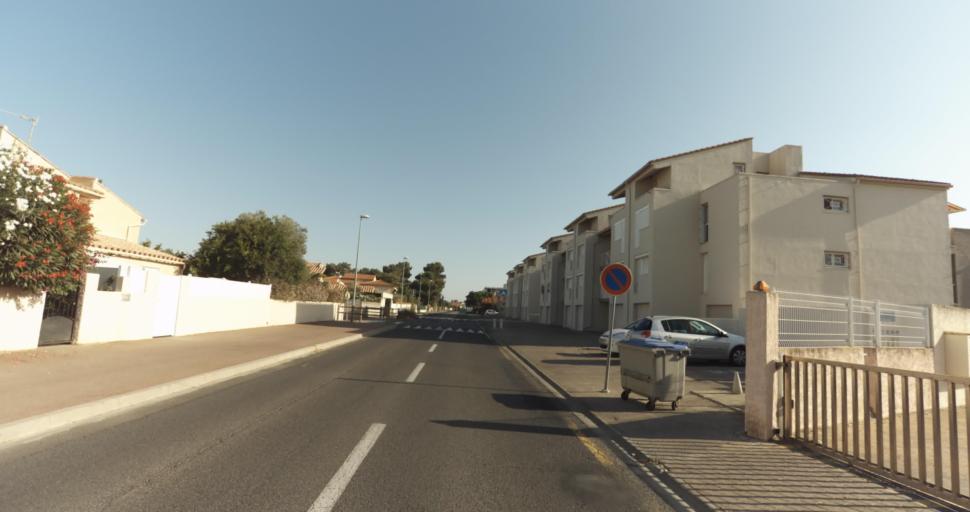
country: FR
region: Languedoc-Roussillon
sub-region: Departement des Pyrenees-Orientales
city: Saint-Cyprien-Plage
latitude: 42.6206
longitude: 3.0330
